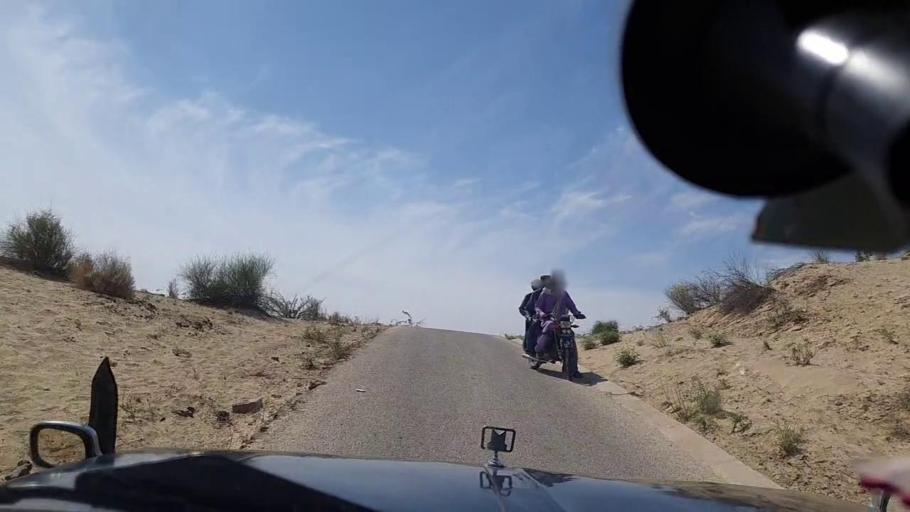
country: PK
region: Sindh
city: Diplo
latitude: 24.3947
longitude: 69.5883
